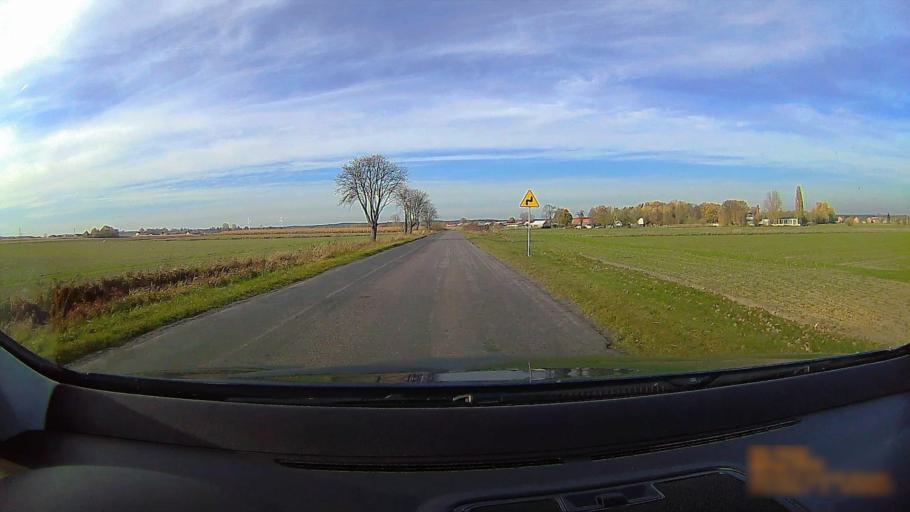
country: PL
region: Greater Poland Voivodeship
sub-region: Powiat ostrzeszowski
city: Doruchow
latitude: 51.4240
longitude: 18.0570
